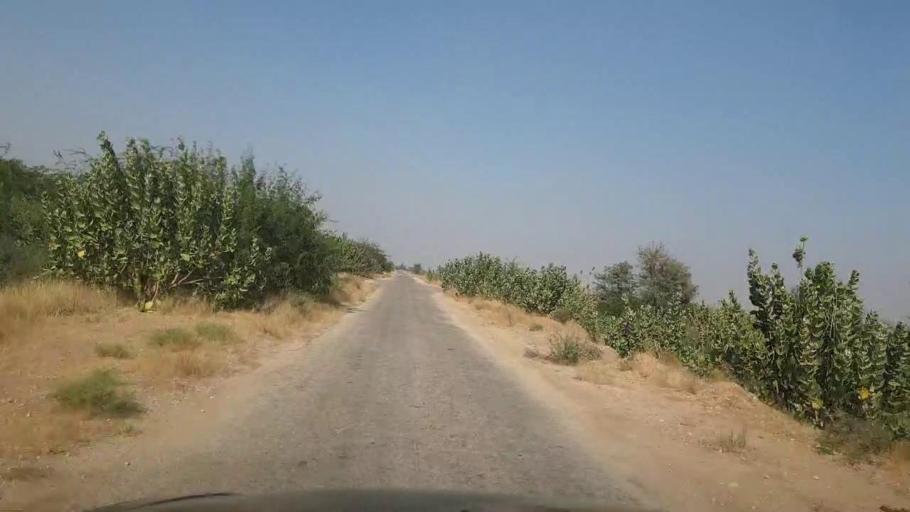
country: PK
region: Sindh
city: Jamshoro
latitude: 25.4786
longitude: 67.8224
